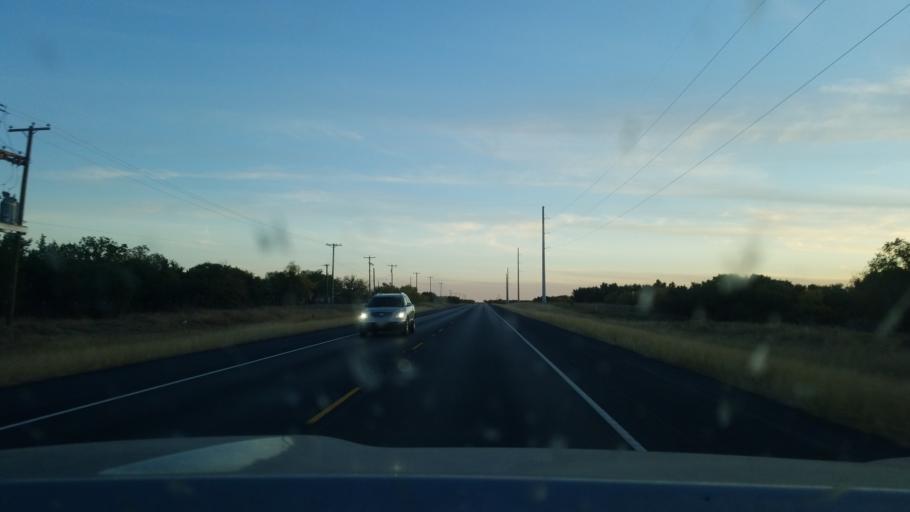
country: US
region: Texas
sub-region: Stephens County
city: Breckenridge
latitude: 32.7021
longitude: -98.9024
